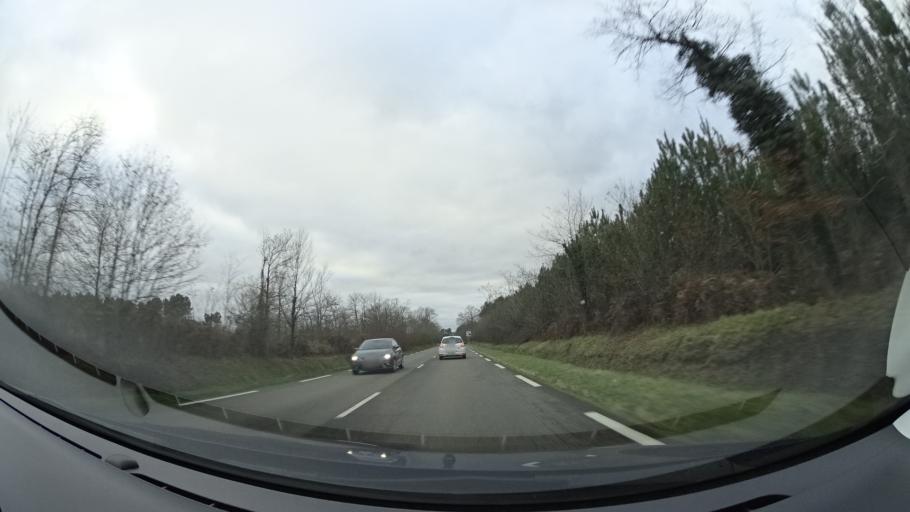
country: FR
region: Aquitaine
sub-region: Departement des Landes
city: Sarbazan
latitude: 43.9730
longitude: -0.2759
